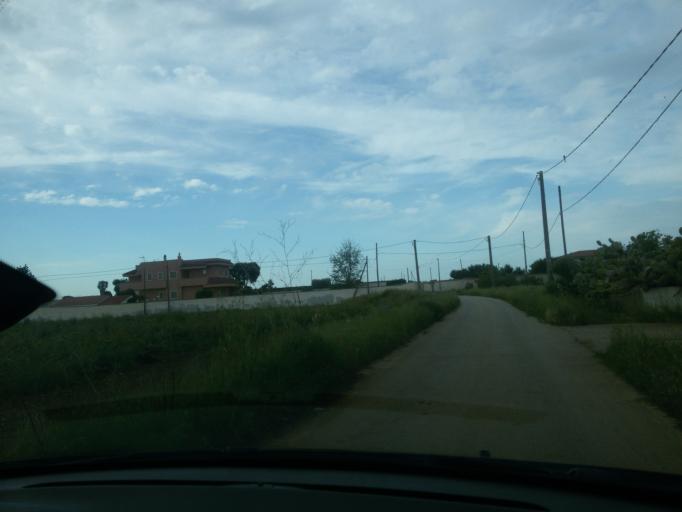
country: IT
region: Apulia
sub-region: Provincia di Brindisi
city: Materdomini
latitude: 40.6618
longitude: 17.9361
